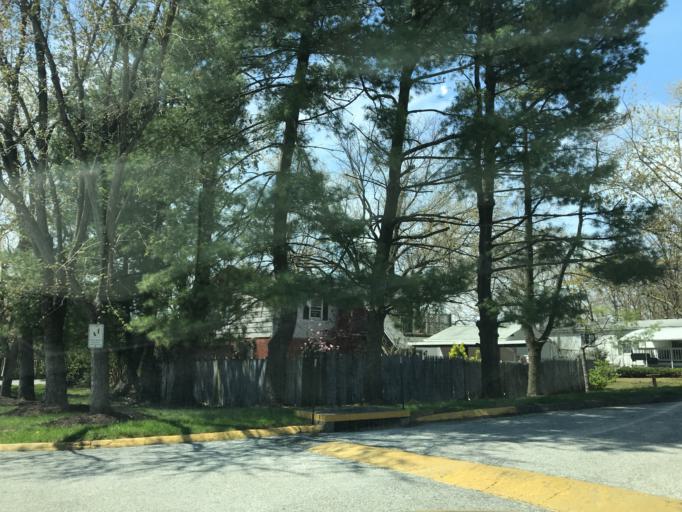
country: US
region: Maryland
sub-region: Baltimore County
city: Rossville
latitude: 39.3292
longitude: -76.4603
